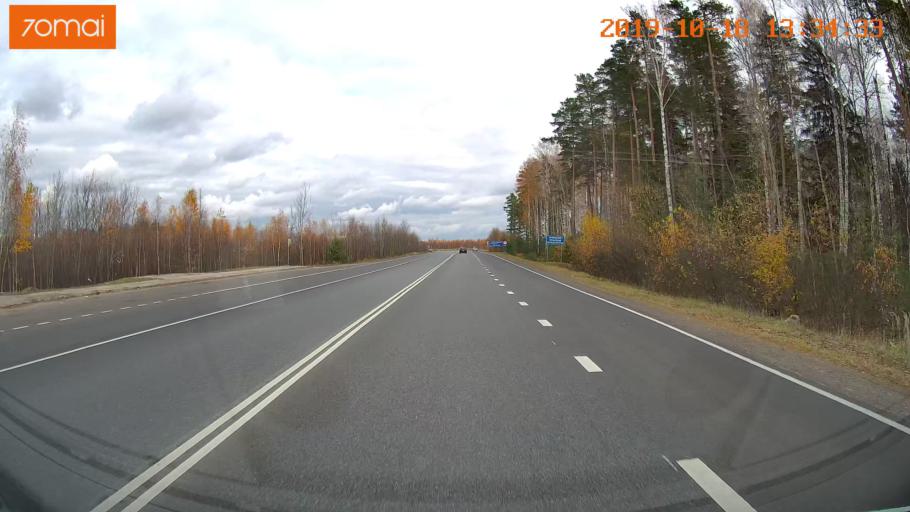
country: RU
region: Rjazan
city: Solotcha
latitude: 54.8550
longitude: 39.9572
